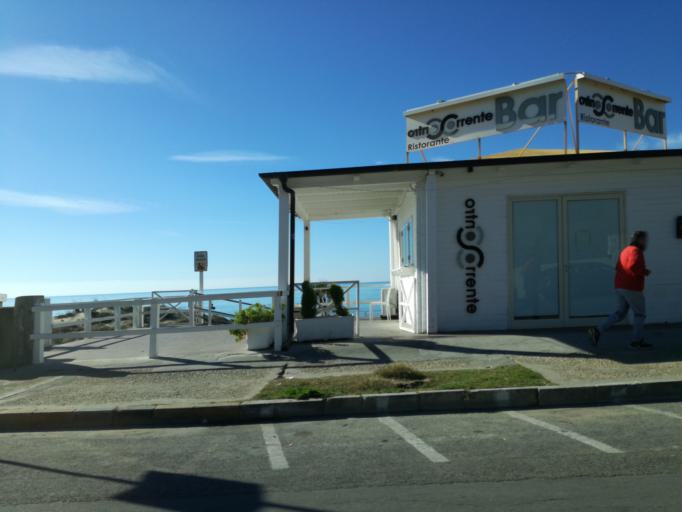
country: IT
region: Sicily
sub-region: Provincia di Caltanissetta
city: Gela
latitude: 37.0707
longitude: 14.2216
